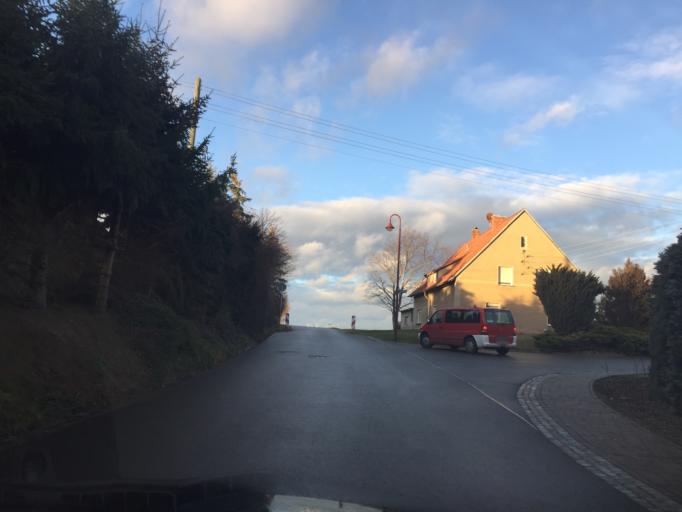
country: DE
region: Thuringia
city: Vollmershain
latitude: 50.8675
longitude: 12.3177
